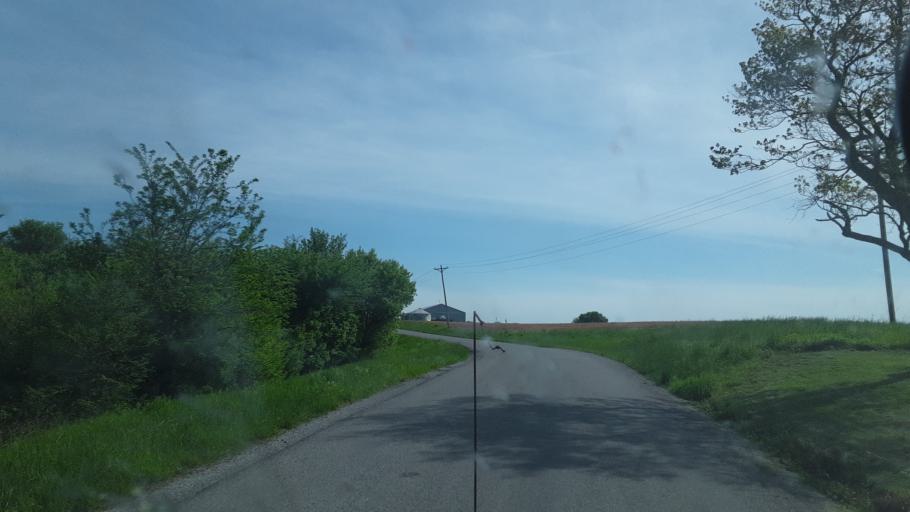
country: US
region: Illinois
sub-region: Jackson County
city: Carbondale
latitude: 37.6773
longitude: -89.2959
